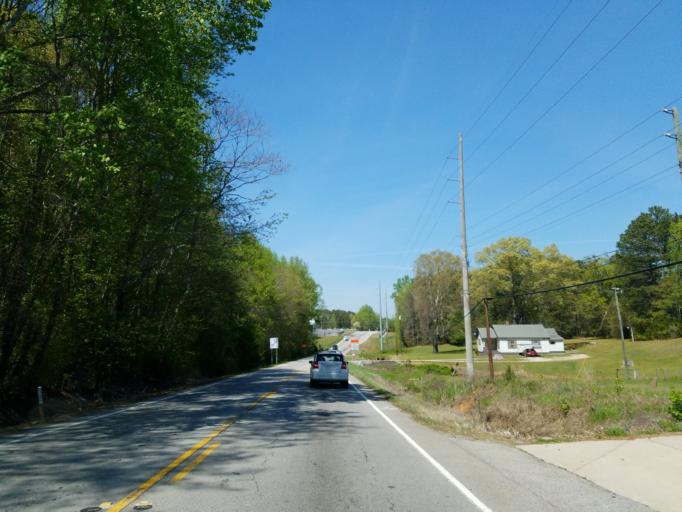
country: US
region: Georgia
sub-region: Paulding County
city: Dallas
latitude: 33.8716
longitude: -84.8416
